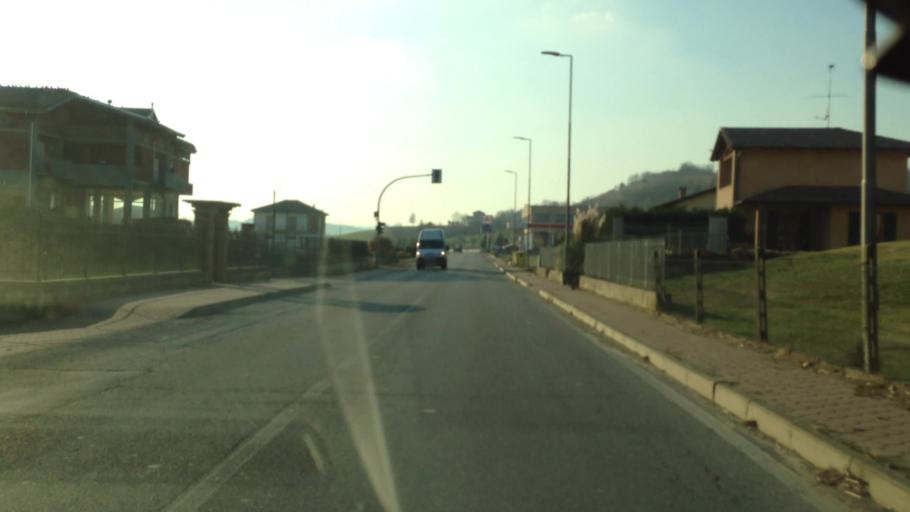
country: IT
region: Piedmont
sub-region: Provincia di Asti
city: Mombercelli
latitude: 44.8233
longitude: 8.2870
